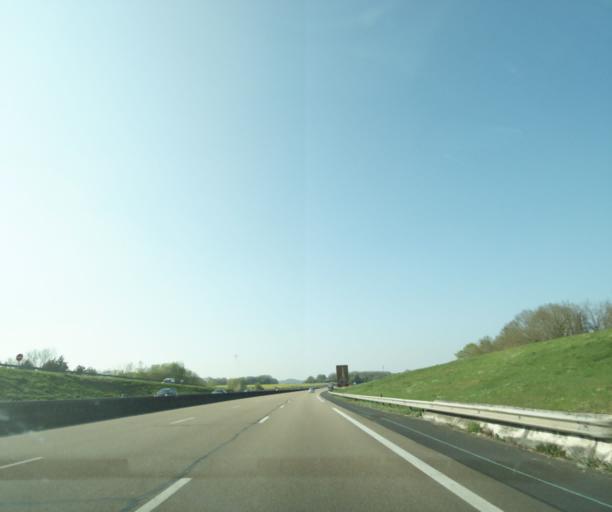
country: FR
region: Ile-de-France
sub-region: Departement de Seine-et-Marne
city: Cely
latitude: 48.4572
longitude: 2.5206
